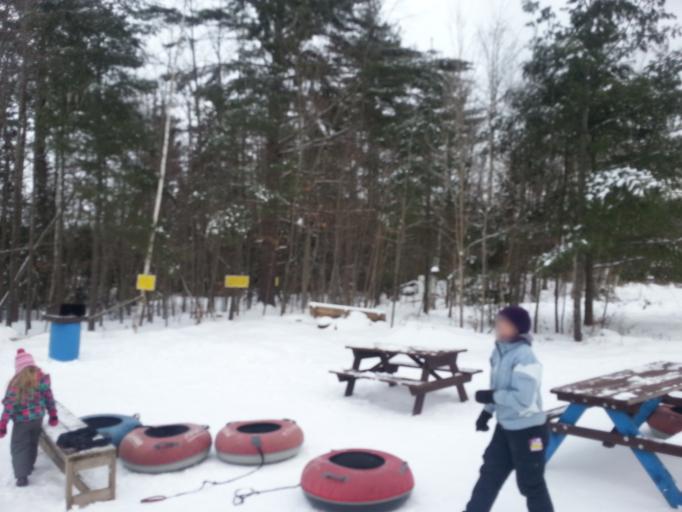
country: CA
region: Ontario
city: Arnprior
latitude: 45.3243
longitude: -76.3320
